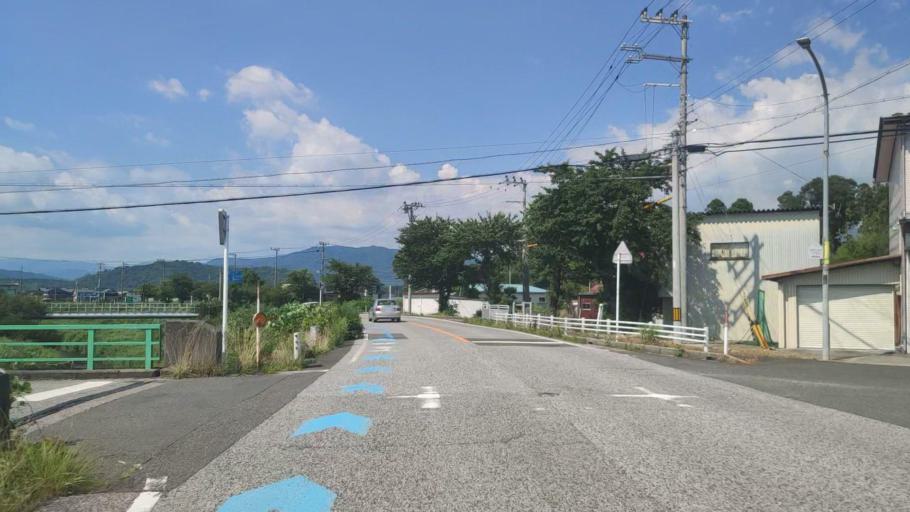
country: JP
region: Shiga Prefecture
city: Nagahama
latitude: 35.4719
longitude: 136.2130
